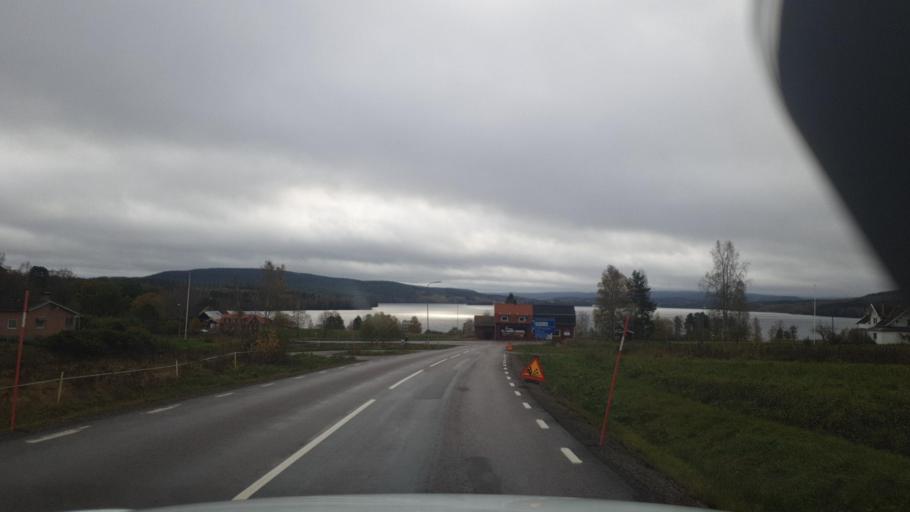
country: SE
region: Vaermland
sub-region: Eda Kommun
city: Amotfors
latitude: 59.7748
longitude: 12.2748
